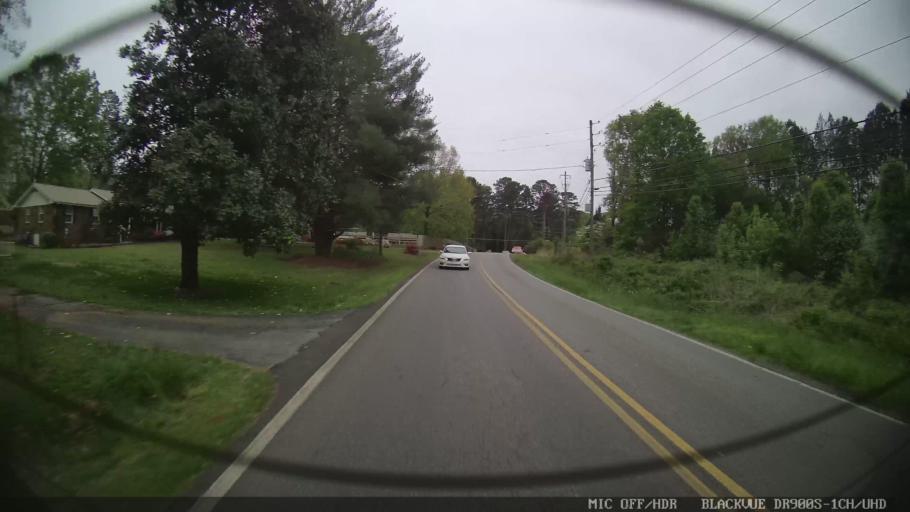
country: US
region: Georgia
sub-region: Bartow County
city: Cartersville
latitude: 34.1976
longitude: -84.7850
